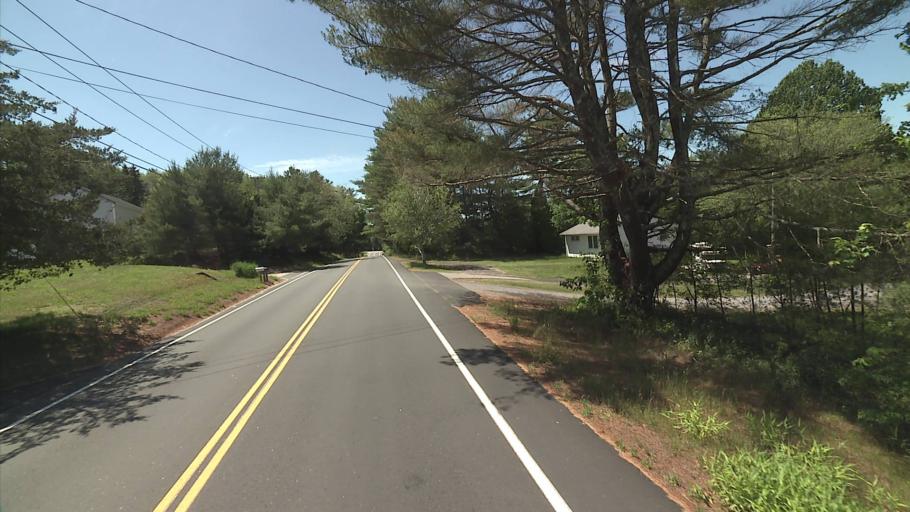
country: US
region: Connecticut
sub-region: Windham County
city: Plainfield
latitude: 41.5798
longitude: -71.8537
